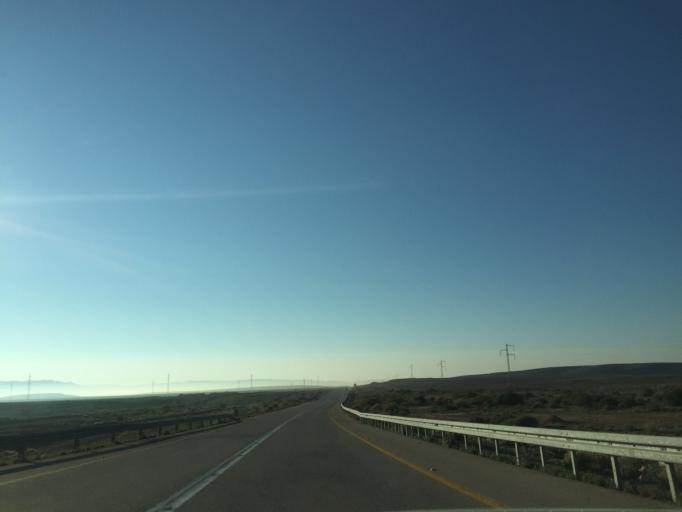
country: IL
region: Southern District
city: Mitzpe Ramon
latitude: 30.4804
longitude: 34.9308
